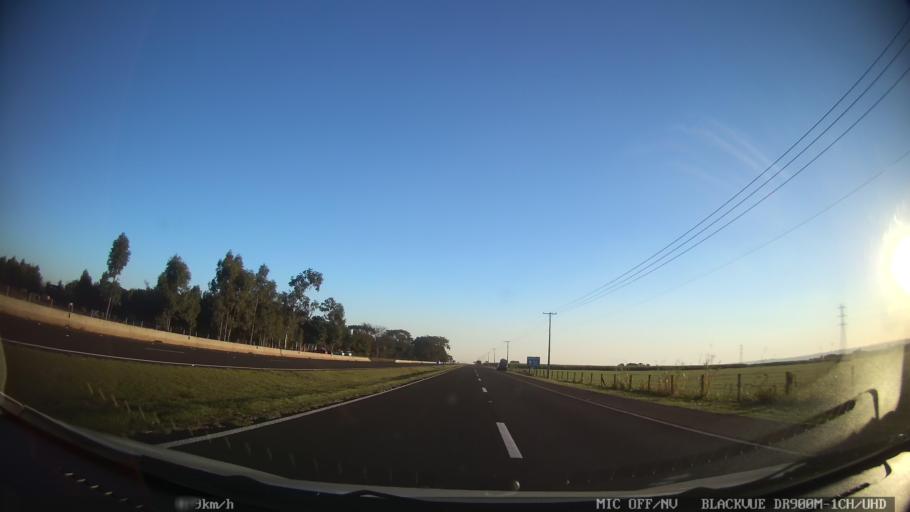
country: BR
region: Sao Paulo
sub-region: Araraquara
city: Araraquara
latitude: -21.8106
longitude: -48.1983
